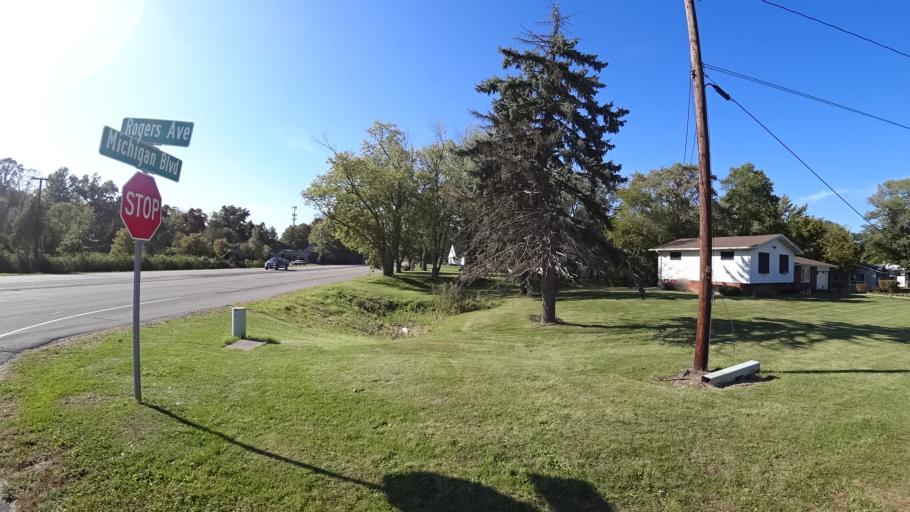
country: US
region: Indiana
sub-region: LaPorte County
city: Trail Creek
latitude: 41.7016
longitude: -86.8406
